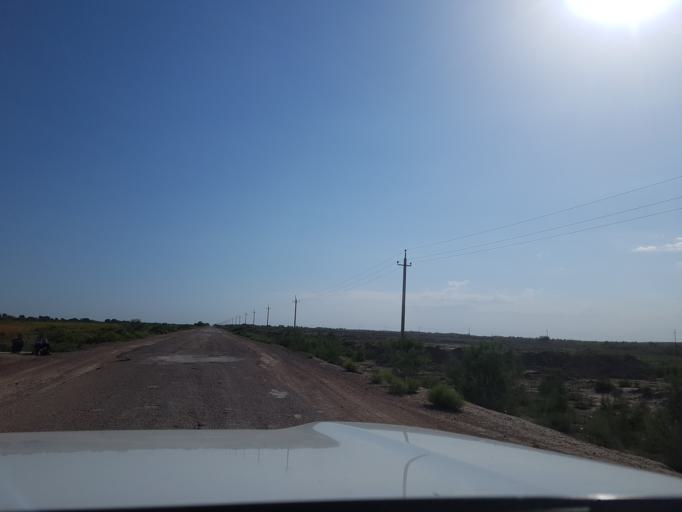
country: TM
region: Dasoguz
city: Koeneuergench
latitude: 42.0324
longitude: 58.8045
